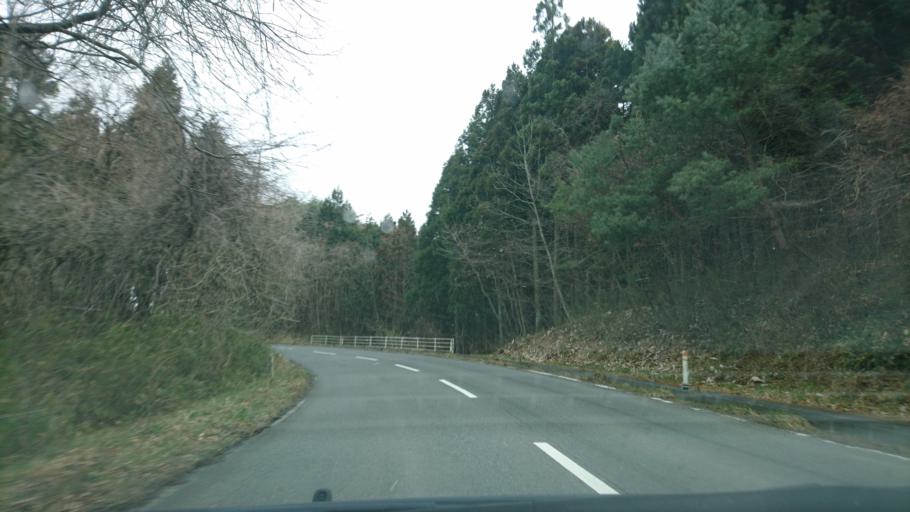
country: JP
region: Iwate
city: Ichinoseki
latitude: 38.8320
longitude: 141.1715
